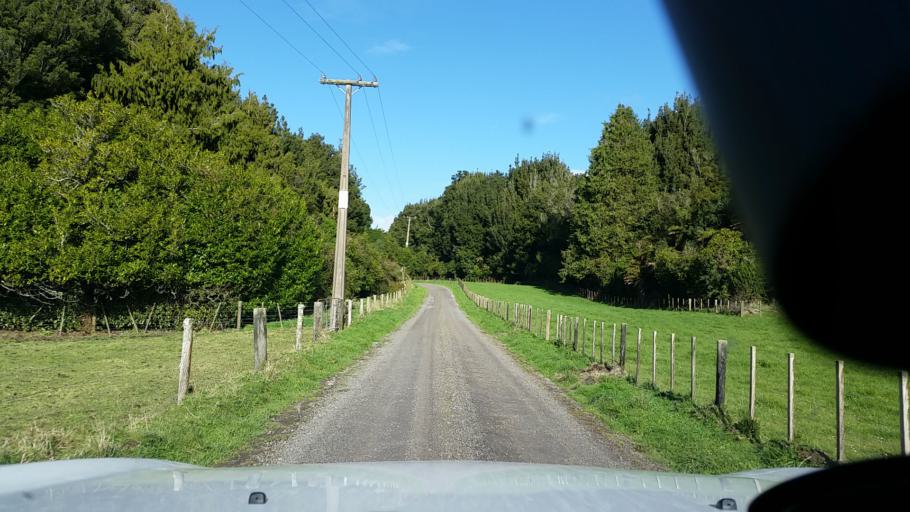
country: NZ
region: Bay of Plenty
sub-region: Rotorua District
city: Rotorua
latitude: -38.1009
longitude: 176.0676
